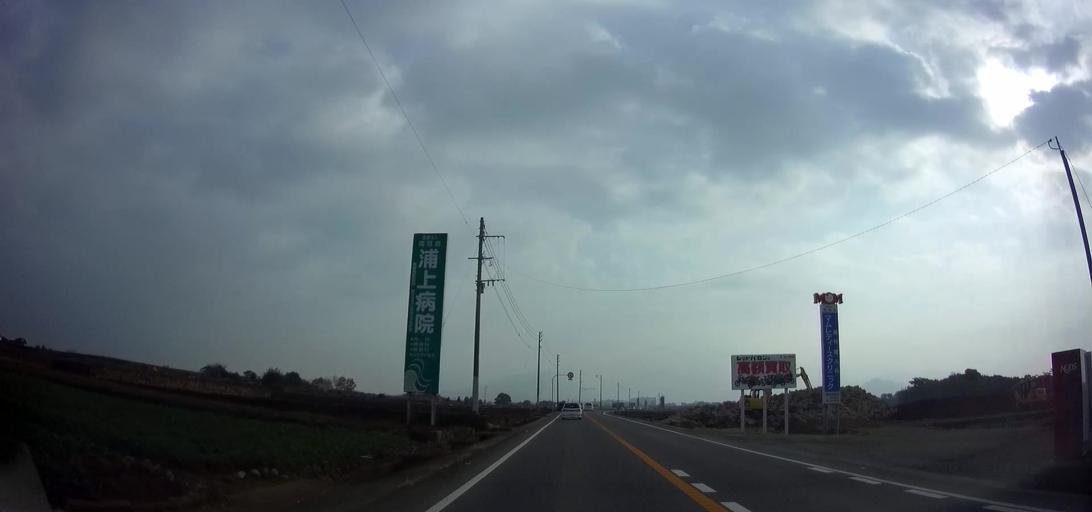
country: JP
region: Nagasaki
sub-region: Isahaya-shi
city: Isahaya
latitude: 32.7981
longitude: 130.1489
